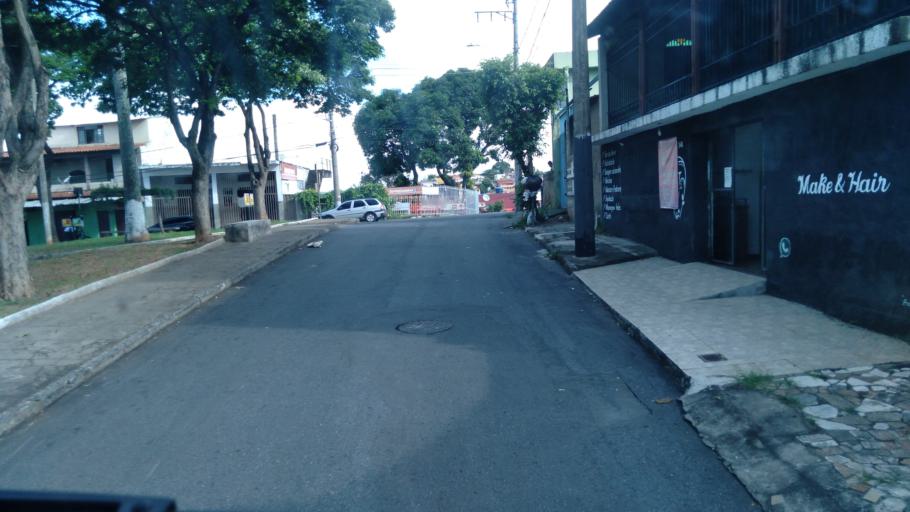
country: BR
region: Minas Gerais
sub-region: Belo Horizonte
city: Belo Horizonte
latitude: -19.8515
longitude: -43.9107
